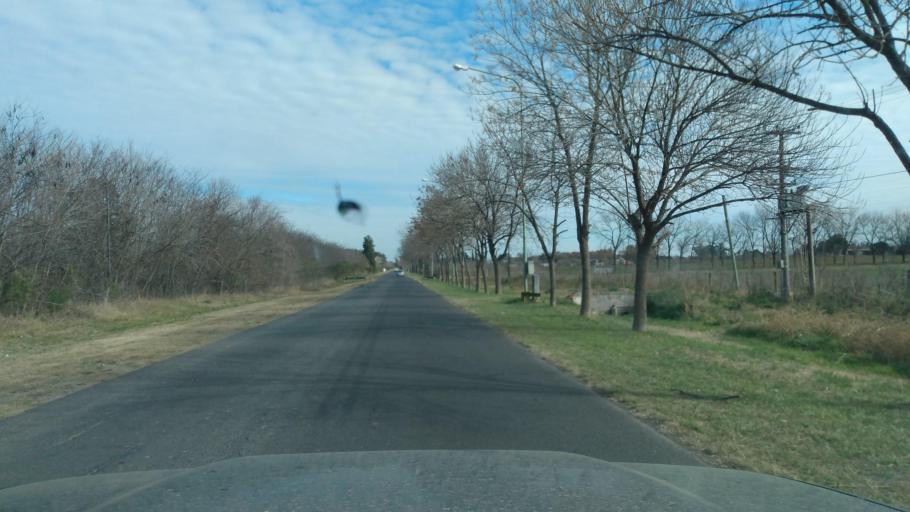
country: AR
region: Buenos Aires
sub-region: Partido de Lujan
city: Lujan
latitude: -34.5760
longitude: -59.1642
